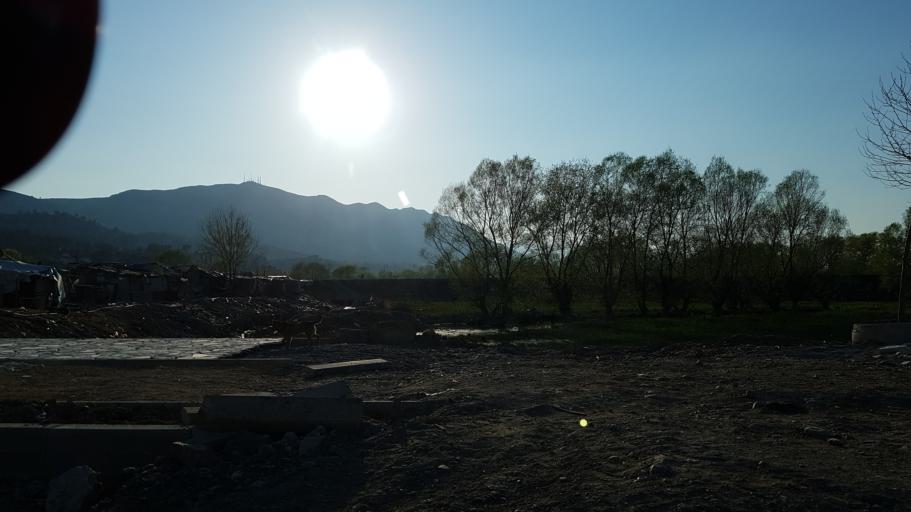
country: AL
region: Shkoder
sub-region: Rrethi i Shkodres
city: Shkoder
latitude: 42.0560
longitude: 19.4982
